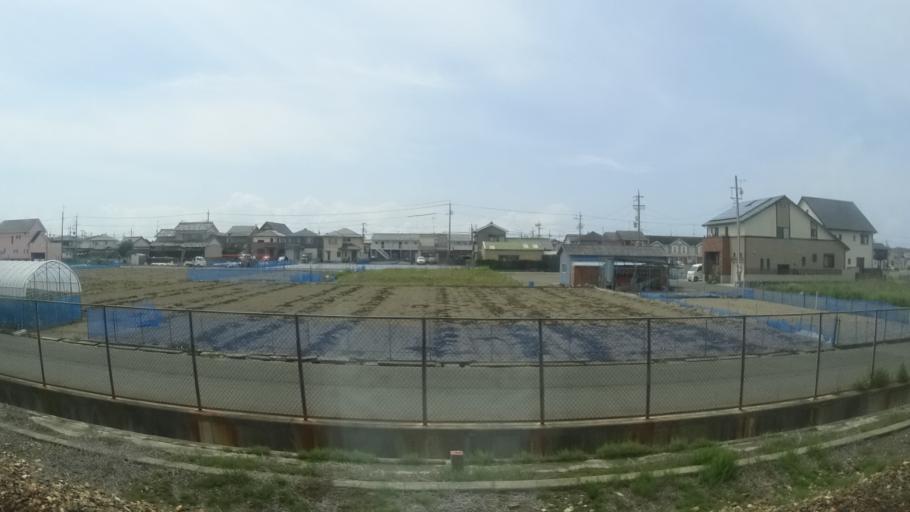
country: JP
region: Shizuoka
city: Hamamatsu
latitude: 34.6855
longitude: 137.6387
